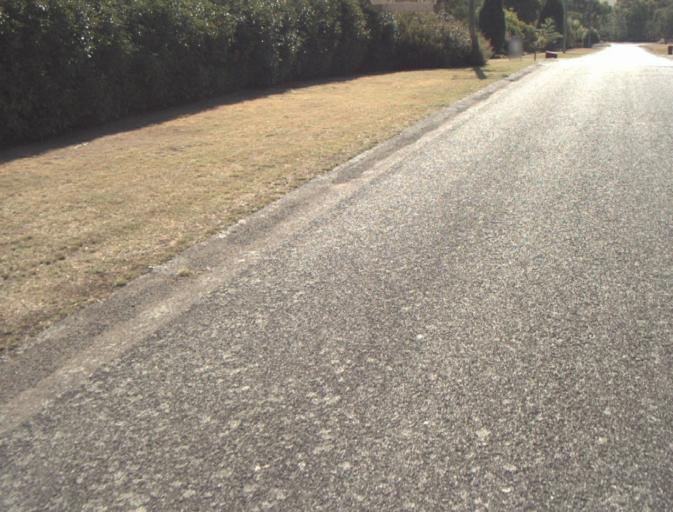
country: AU
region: Tasmania
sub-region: Launceston
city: Mayfield
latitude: -41.3255
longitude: 147.0558
